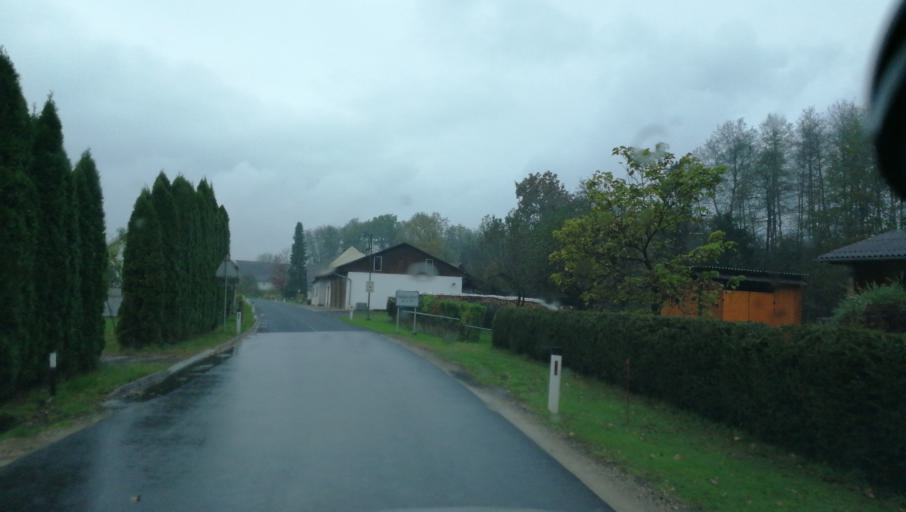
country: AT
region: Styria
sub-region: Politischer Bezirk Leibnitz
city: Spielfeld
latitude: 46.7337
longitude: 15.6712
